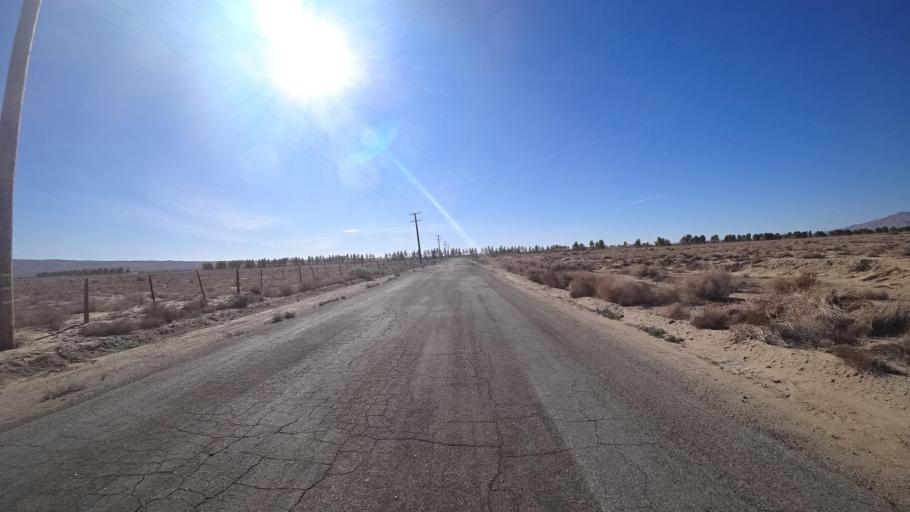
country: US
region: California
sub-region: Kern County
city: California City
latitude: 35.2894
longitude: -117.9506
